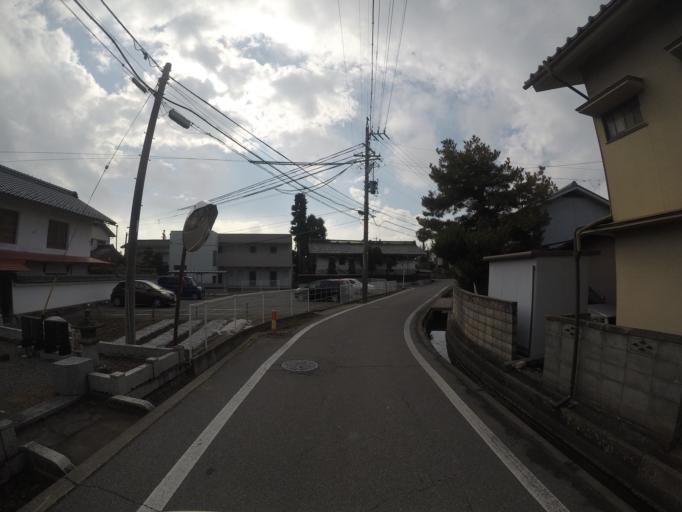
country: JP
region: Nagano
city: Matsumoto
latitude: 36.2195
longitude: 137.9001
